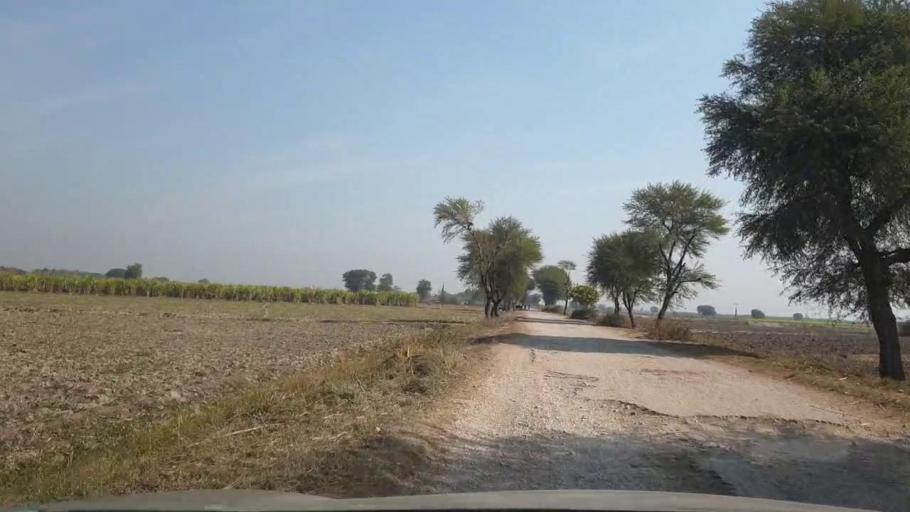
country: PK
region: Sindh
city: Tando Adam
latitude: 25.6379
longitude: 68.7227
